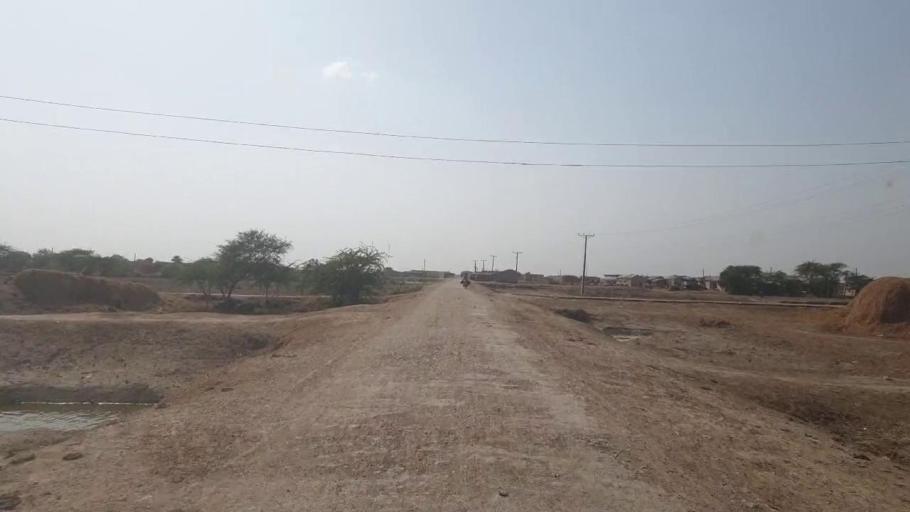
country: PK
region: Sindh
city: Kario
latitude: 24.5151
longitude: 68.5279
